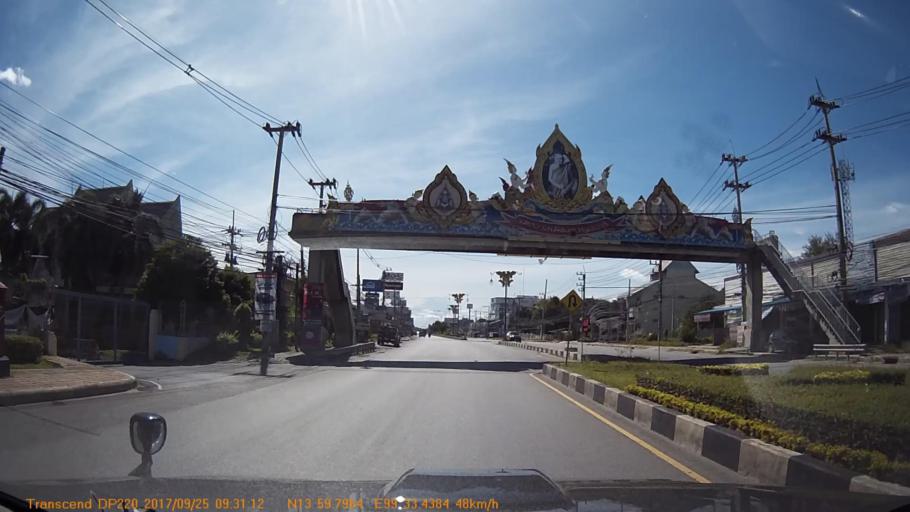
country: TH
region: Kanchanaburi
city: Kanchanaburi
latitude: 13.9965
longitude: 99.5575
